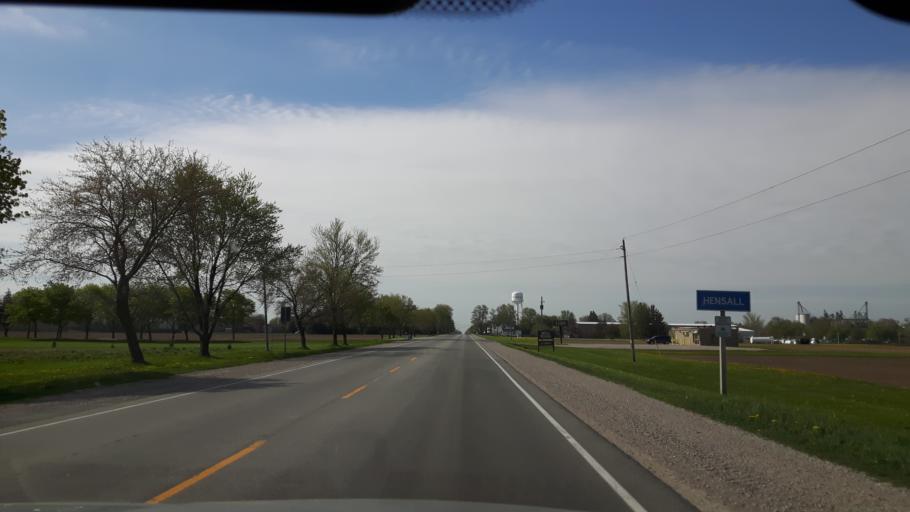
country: CA
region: Ontario
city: Bluewater
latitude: 43.4420
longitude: -81.5002
